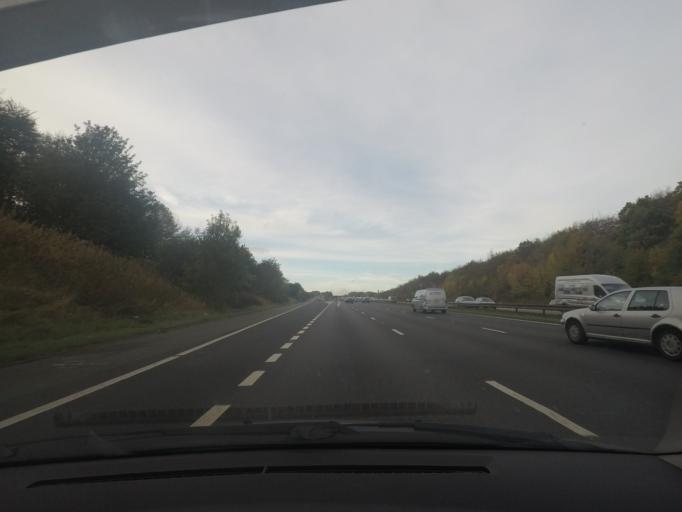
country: GB
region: England
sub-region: Barnsley
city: Stainborough
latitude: 53.5405
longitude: -1.5091
